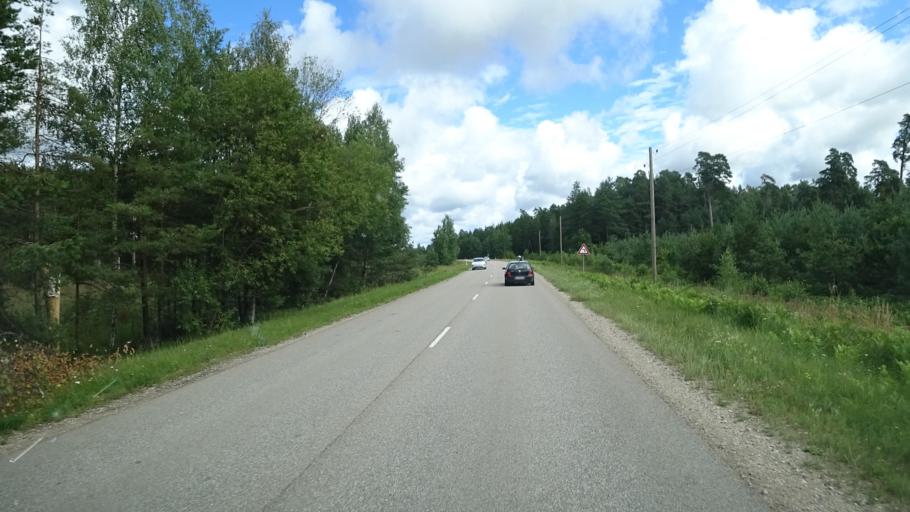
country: LV
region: Grobina
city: Grobina
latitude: 56.6915
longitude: 21.1581
